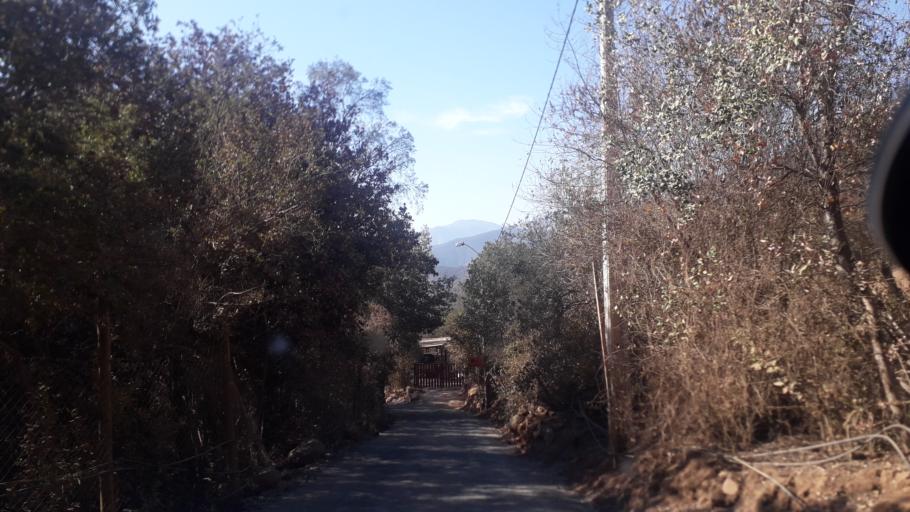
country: CL
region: Valparaiso
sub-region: Provincia de Marga Marga
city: Limache
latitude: -33.0829
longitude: -71.1009
